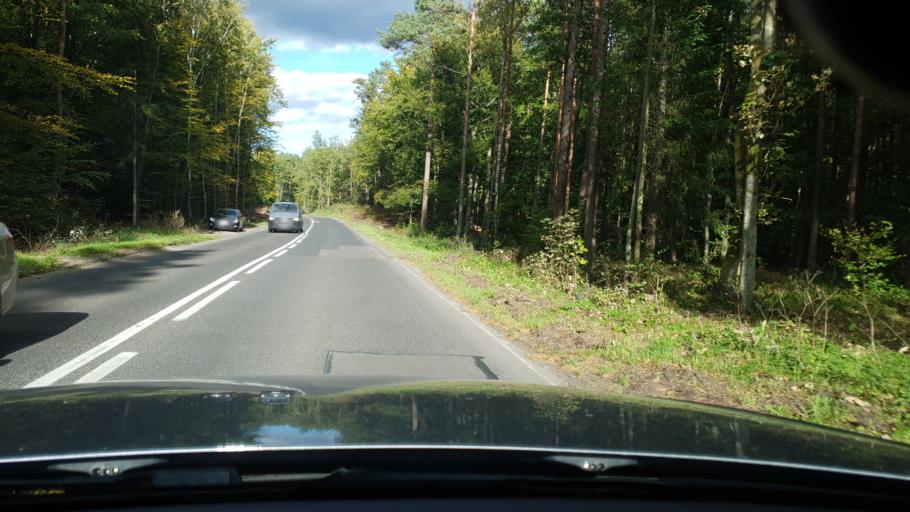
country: PL
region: Pomeranian Voivodeship
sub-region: Powiat wejherowski
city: Koleczkowo
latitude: 54.5014
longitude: 18.3648
